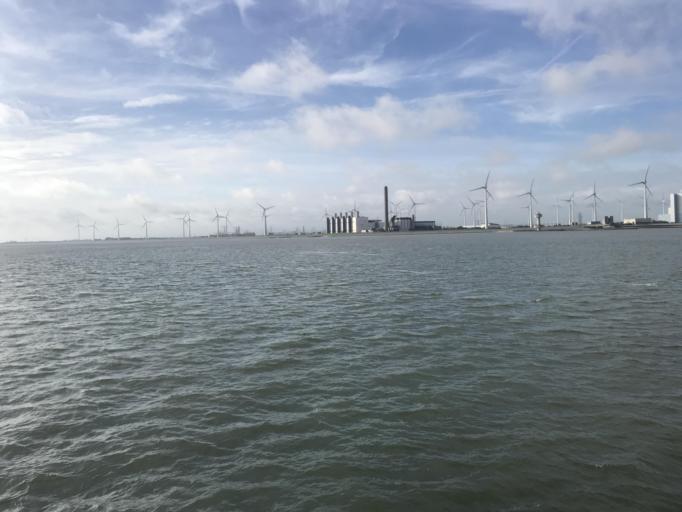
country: NL
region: Groningen
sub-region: Gemeente Delfzijl
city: Delfzijl
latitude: 53.4446
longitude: 6.8985
